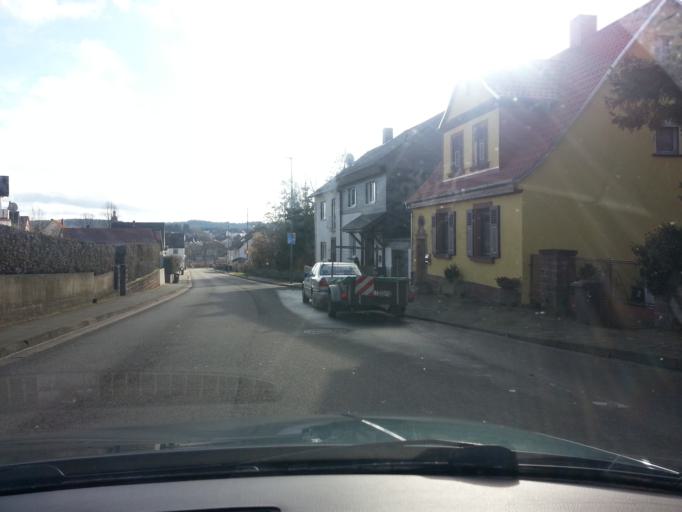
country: DE
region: Rheinland-Pfalz
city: Katzweiler
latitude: 49.4702
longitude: 7.6842
